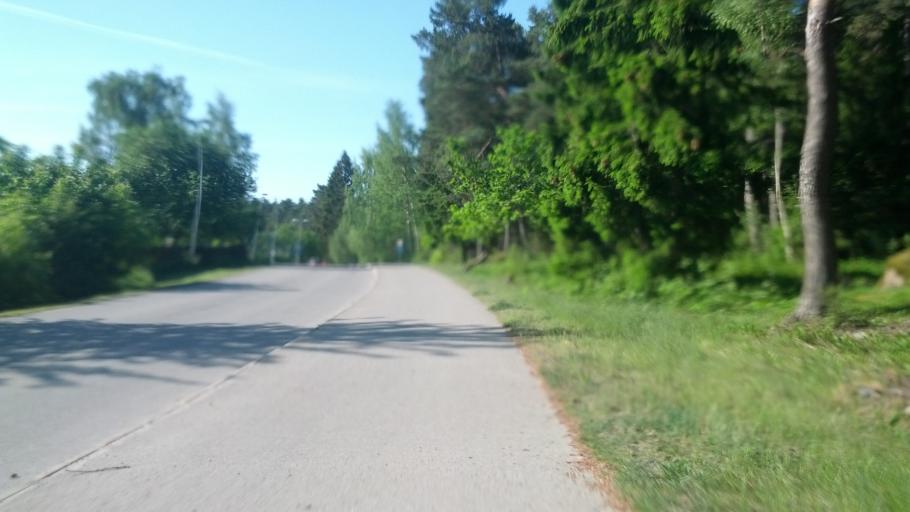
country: SE
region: Stockholm
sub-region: Taby Kommun
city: Taby
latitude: 59.4675
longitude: 18.0467
